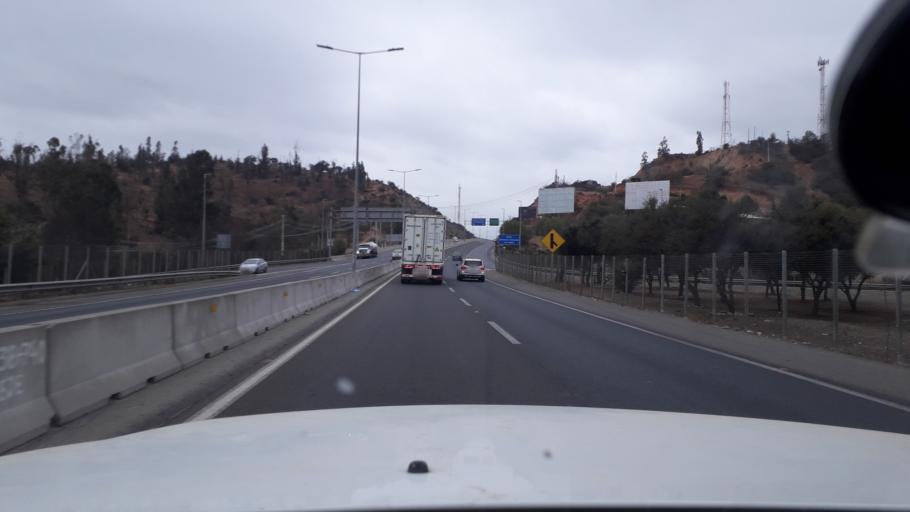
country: CL
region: Valparaiso
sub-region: Provincia de Marga Marga
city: Villa Alemana
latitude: -33.0518
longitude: -71.3323
